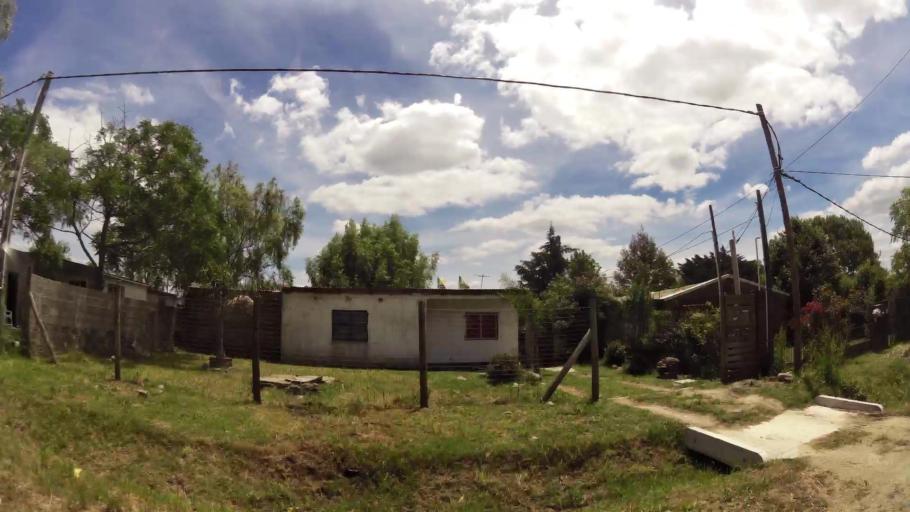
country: UY
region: Canelones
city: Colonia Nicolich
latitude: -34.8170
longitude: -55.9747
